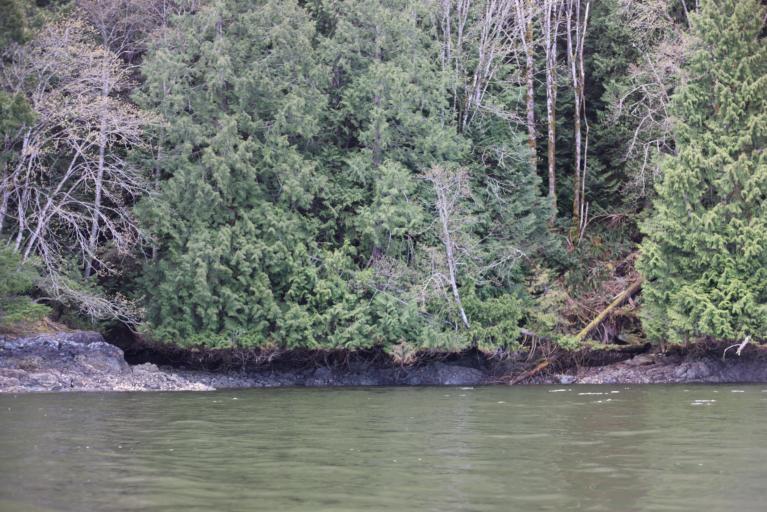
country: CA
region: British Columbia
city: Langford
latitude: 48.5509
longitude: -123.5173
